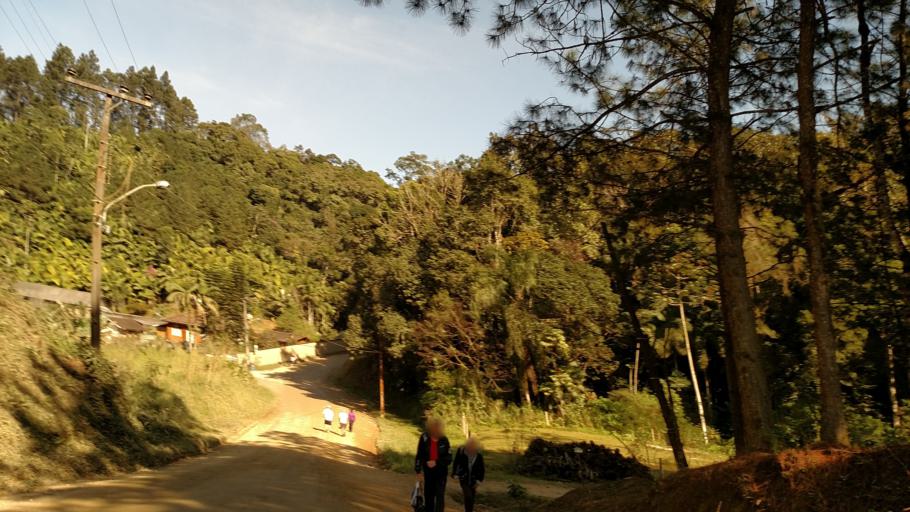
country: BR
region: Santa Catarina
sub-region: Pomerode
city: Pomerode
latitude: -26.7352
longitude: -49.0736
